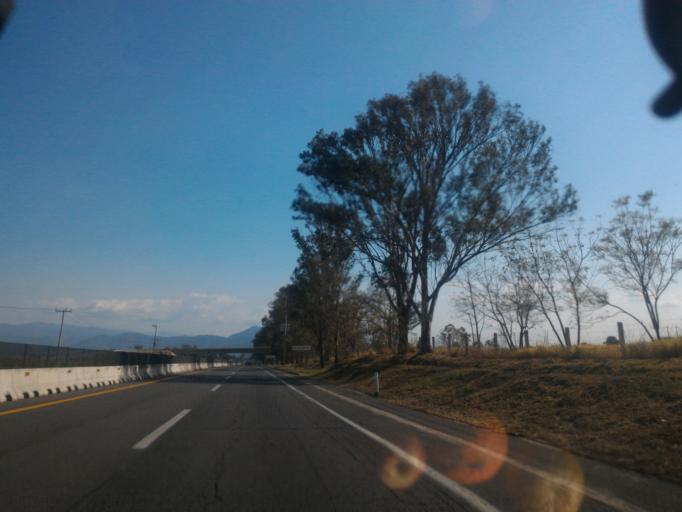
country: MX
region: Jalisco
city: Zapotiltic
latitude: 19.5750
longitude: -103.4458
